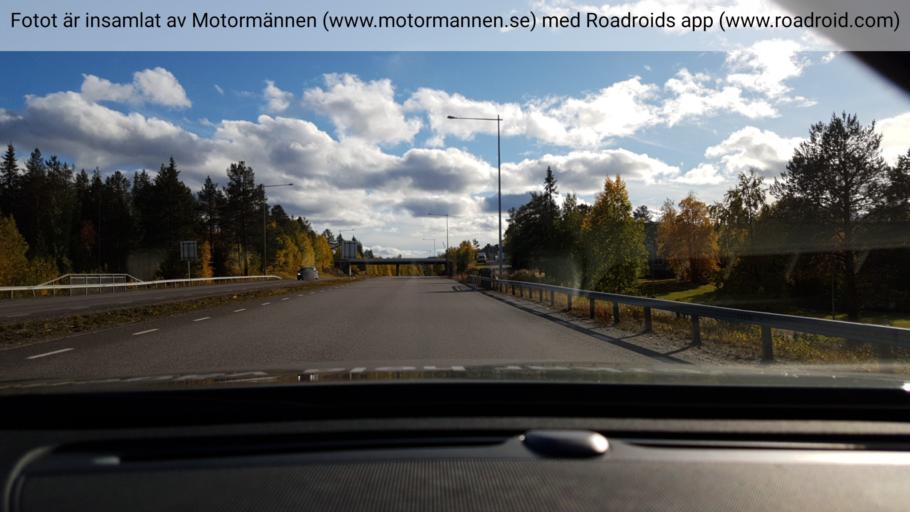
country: SE
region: Norrbotten
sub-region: Gallivare Kommun
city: Gaellivare
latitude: 67.1443
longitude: 20.6630
